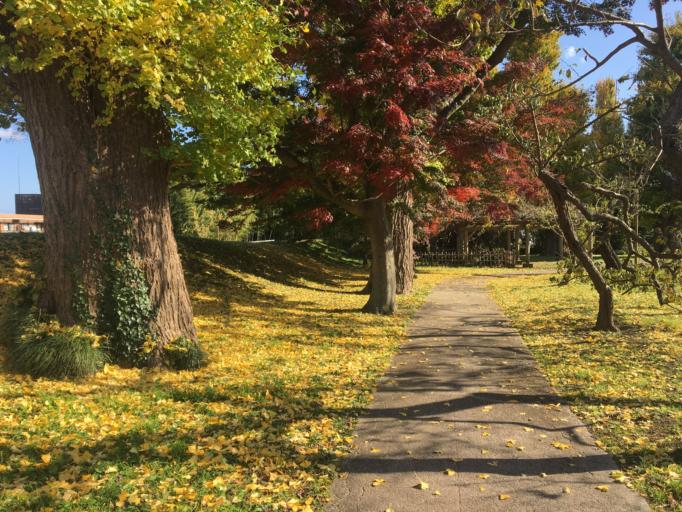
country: JP
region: Ibaraki
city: Mito-shi
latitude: 36.3762
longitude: 140.4776
